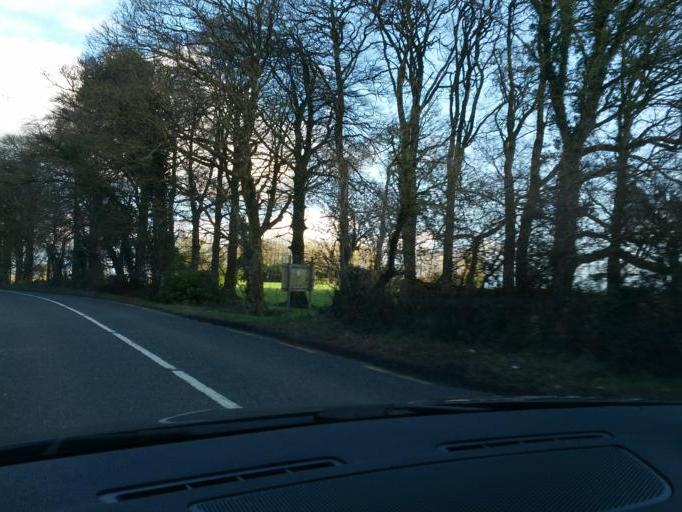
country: IE
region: Connaught
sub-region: Roscommon
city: Roscommon
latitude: 53.6696
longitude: -8.3338
